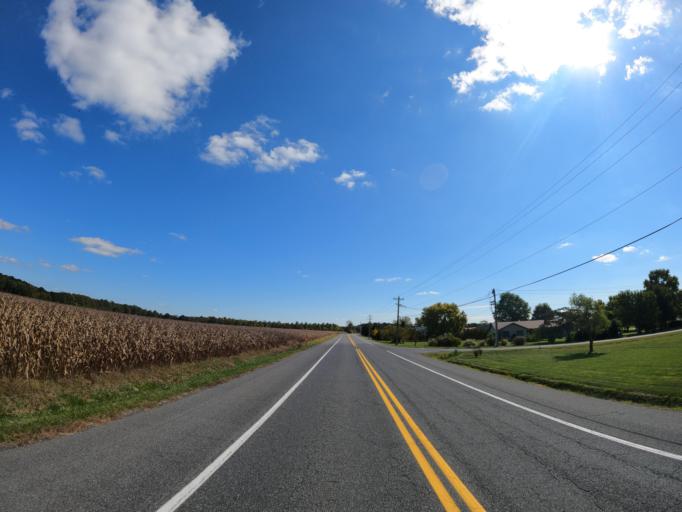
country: US
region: Delaware
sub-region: Sussex County
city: Bridgeville
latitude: 38.8239
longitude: -75.6262
